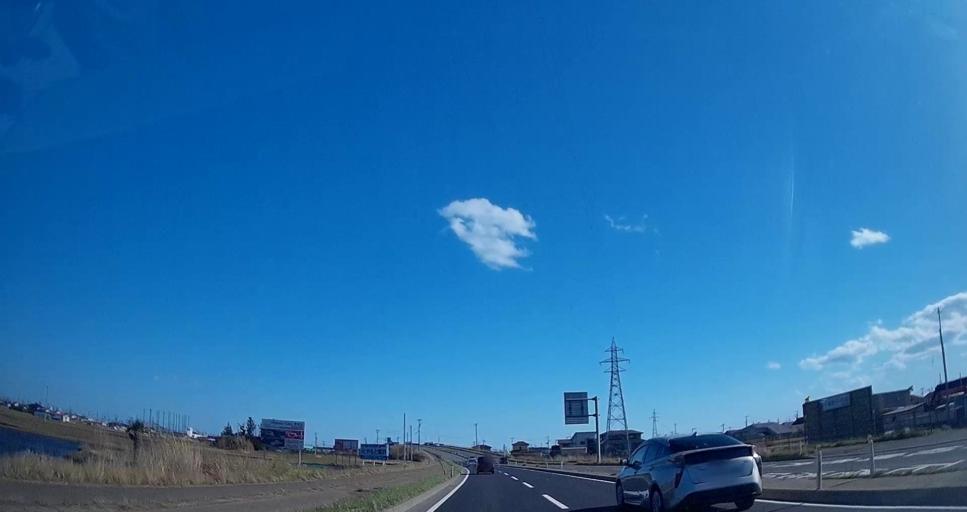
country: JP
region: Miyagi
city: Yamoto
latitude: 38.4370
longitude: 141.2464
